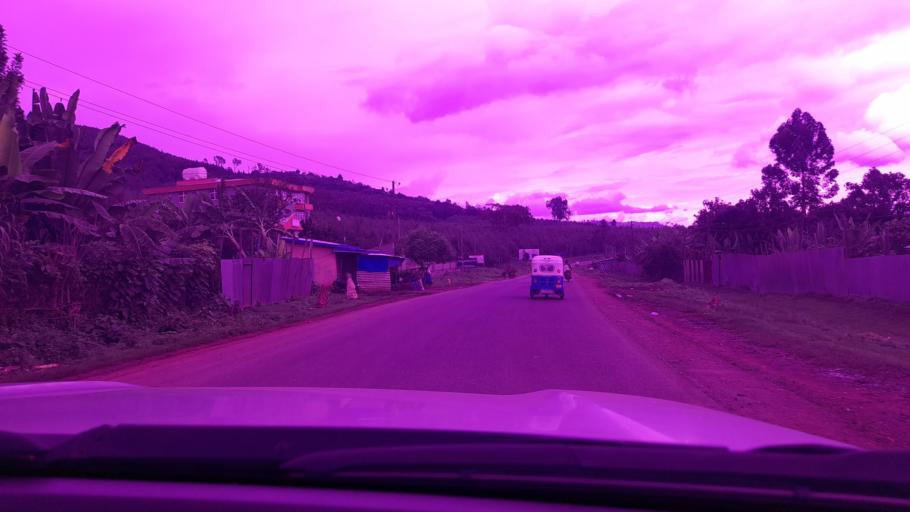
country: ET
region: Oromiya
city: Jima
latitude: 7.6689
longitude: 36.8702
